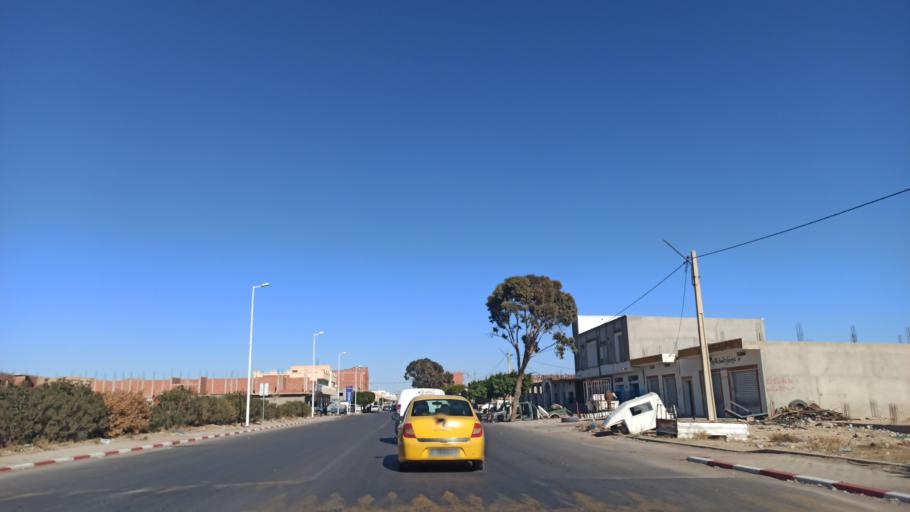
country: TN
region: Sidi Bu Zayd
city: Bi'r al Hufayy
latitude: 34.9183
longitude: 9.1862
